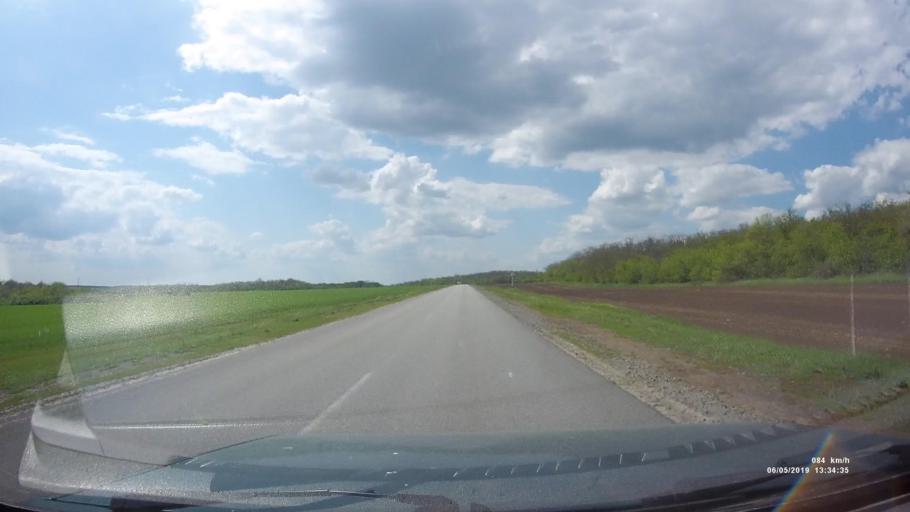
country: RU
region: Rostov
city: Ust'-Donetskiy
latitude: 47.6932
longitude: 40.7602
